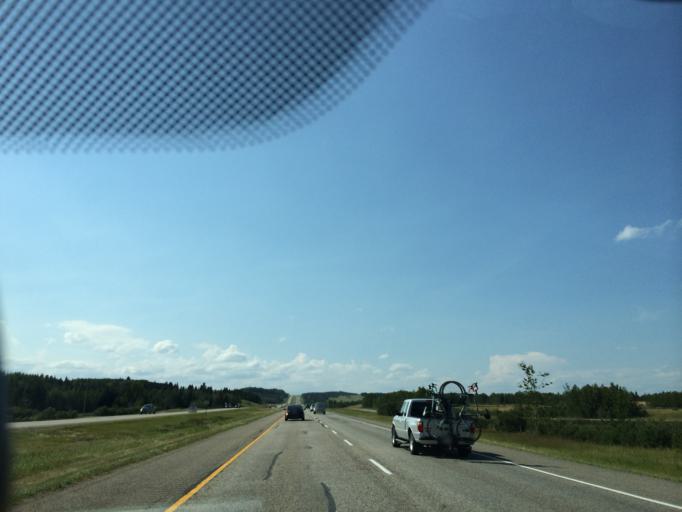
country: CA
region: Alberta
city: Cochrane
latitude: 51.1238
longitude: -114.6755
